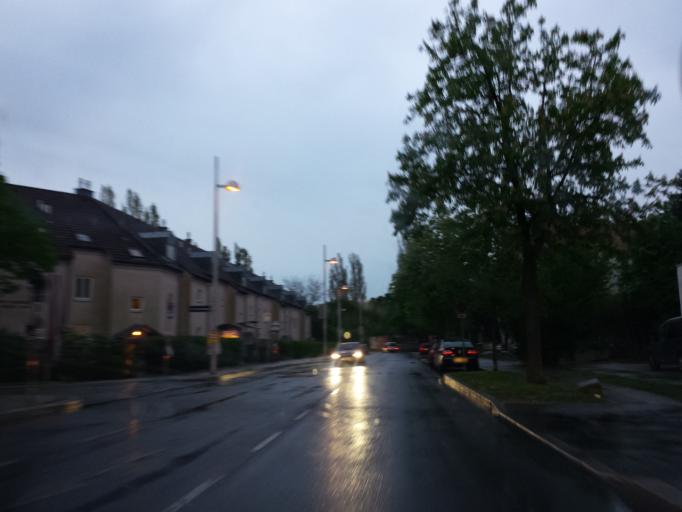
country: AT
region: Lower Austria
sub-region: Politischer Bezirk Modling
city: Perchtoldsdorf
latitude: 48.1379
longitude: 16.2578
